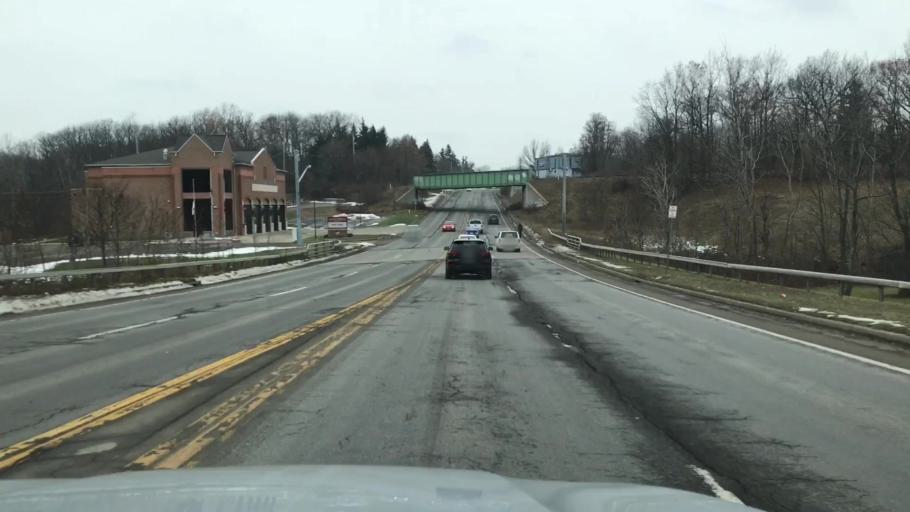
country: US
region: New York
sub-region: Erie County
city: Blasdell
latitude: 42.7906
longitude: -78.7925
